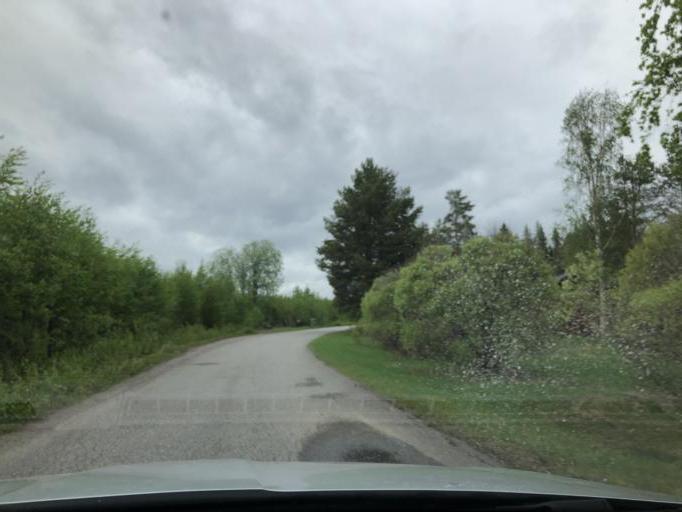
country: SE
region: Norrbotten
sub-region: Pitea Kommun
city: Roknas
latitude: 65.3883
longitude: 21.2698
